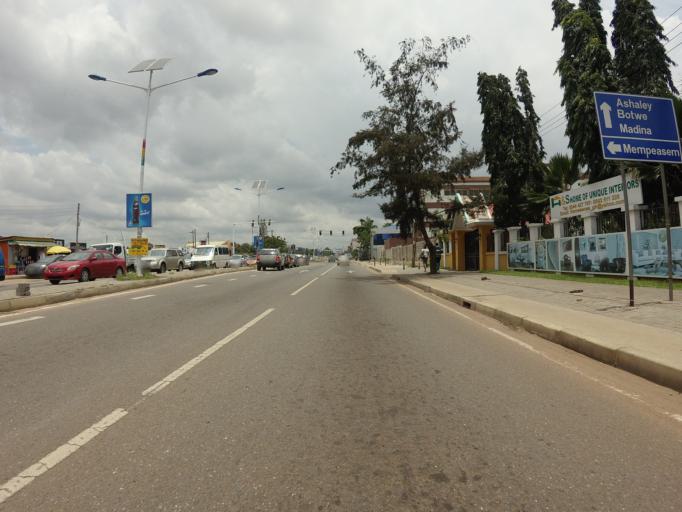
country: GH
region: Greater Accra
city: Medina Estates
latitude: 5.6517
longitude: -0.1506
